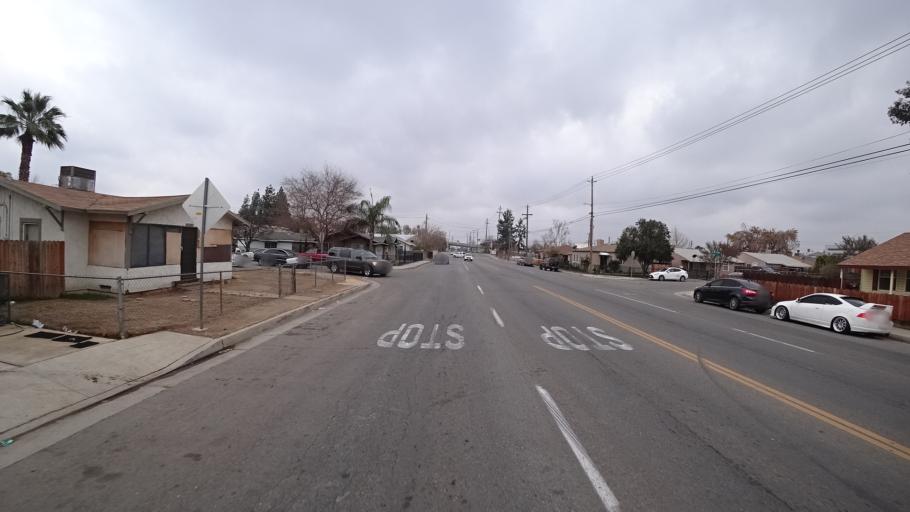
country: US
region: California
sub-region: Kern County
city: Bakersfield
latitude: 35.3854
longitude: -119.0105
